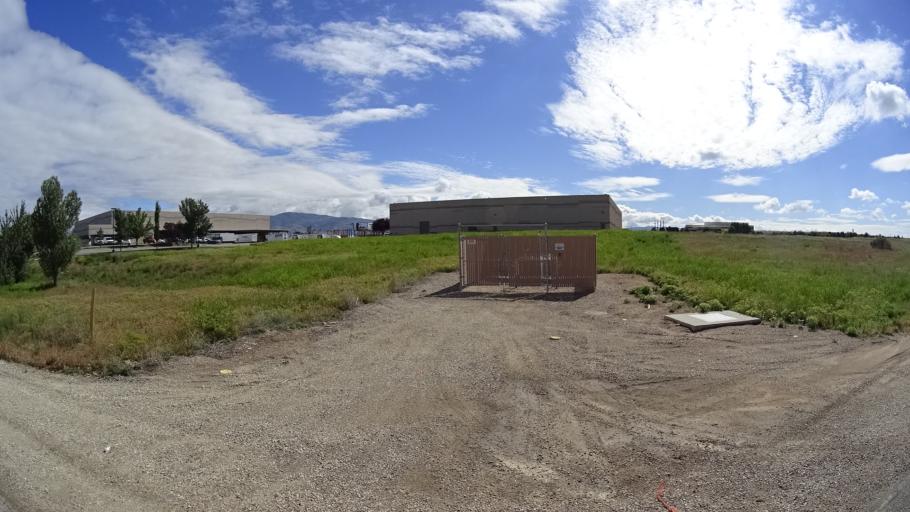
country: US
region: Idaho
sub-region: Ada County
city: Boise
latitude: 43.5313
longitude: -116.1579
